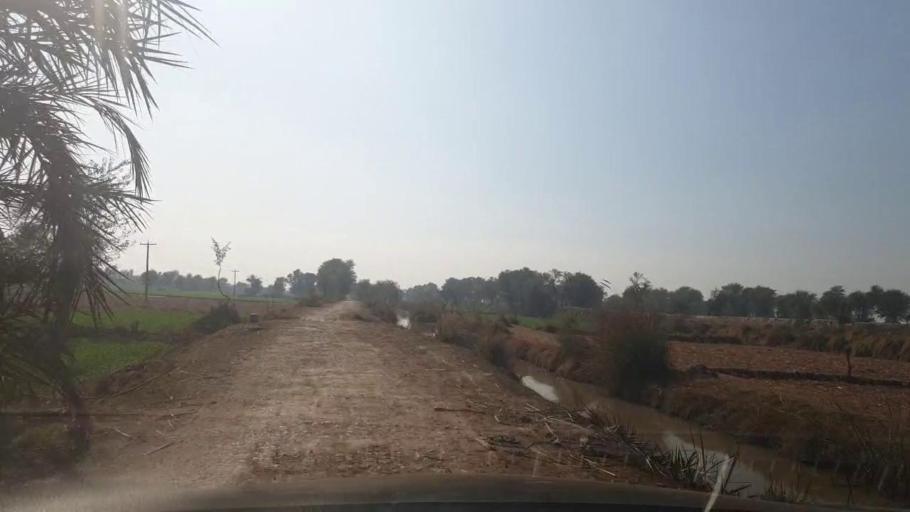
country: PK
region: Sindh
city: Ubauro
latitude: 28.1417
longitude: 69.6861
